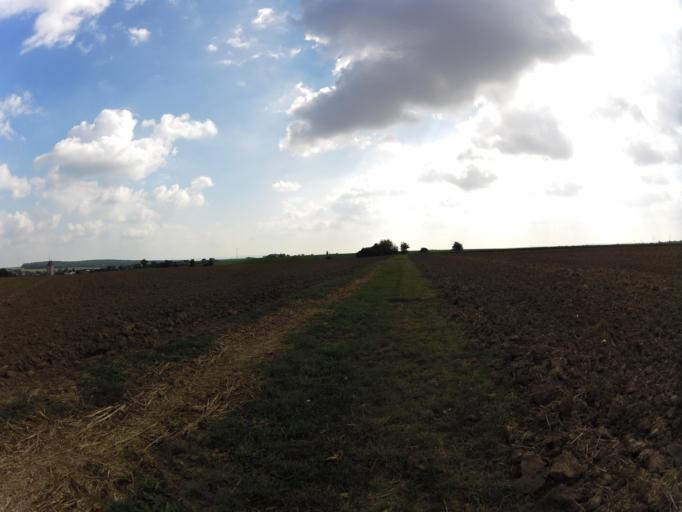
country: DE
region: Bavaria
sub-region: Regierungsbezirk Unterfranken
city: Prosselsheim
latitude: 49.8656
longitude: 10.1135
